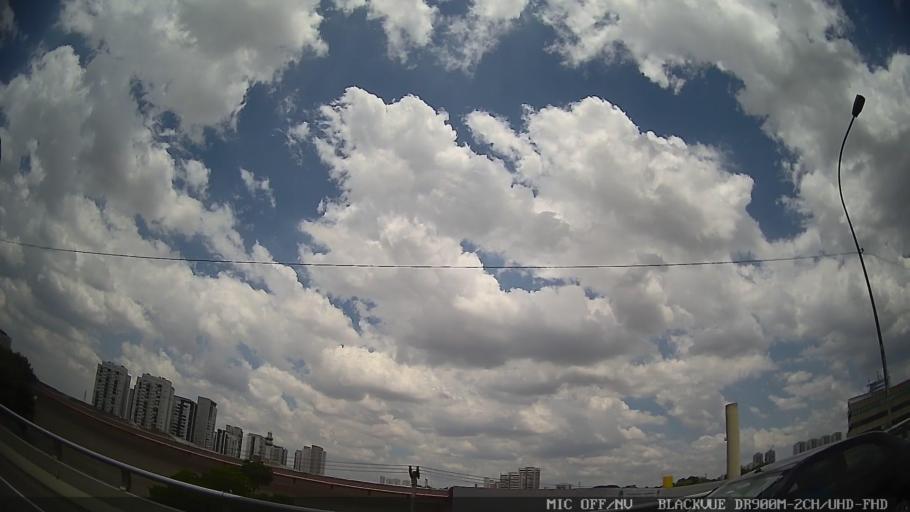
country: BR
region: Sao Paulo
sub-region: Osasco
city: Osasco
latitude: -23.5065
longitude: -46.7202
